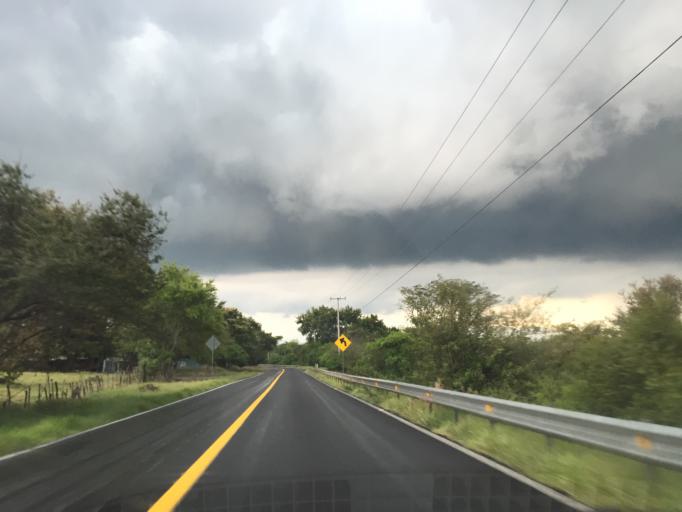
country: MX
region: Colima
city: Cuauhtemoc
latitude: 19.3491
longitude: -103.5811
